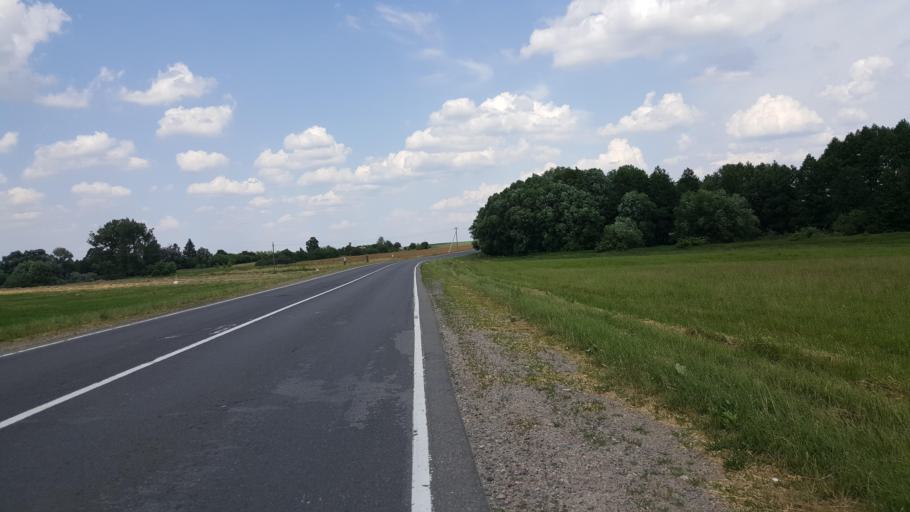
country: BY
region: Brest
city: Kamyanyets
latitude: 52.4026
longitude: 23.7842
